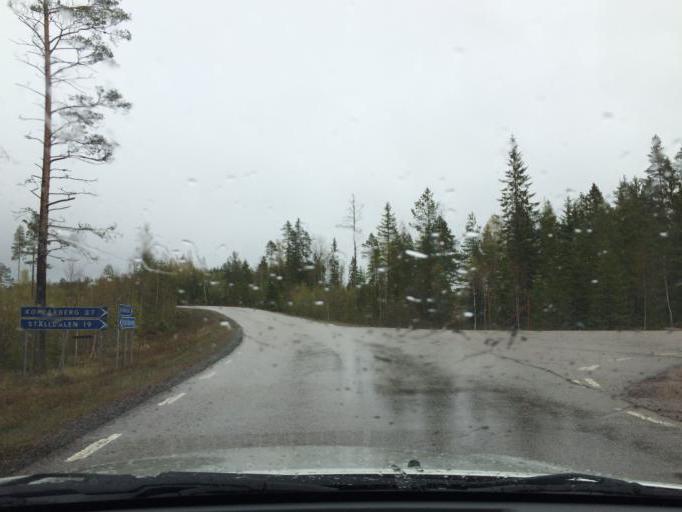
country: SE
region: Dalarna
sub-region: Ludvika Kommun
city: Abborrberget
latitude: 60.0472
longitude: 14.7845
